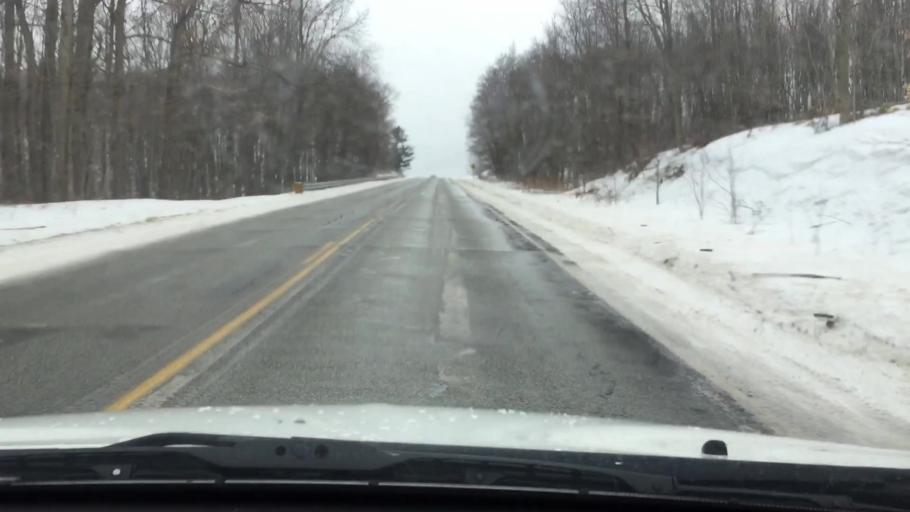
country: US
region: Michigan
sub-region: Wexford County
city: Cadillac
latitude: 44.1689
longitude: -85.4054
